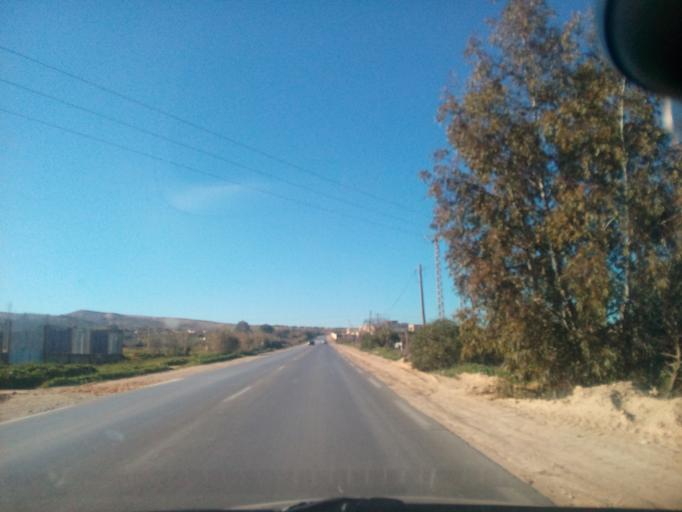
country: DZ
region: Relizane
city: Relizane
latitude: 35.9033
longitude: 0.5204
